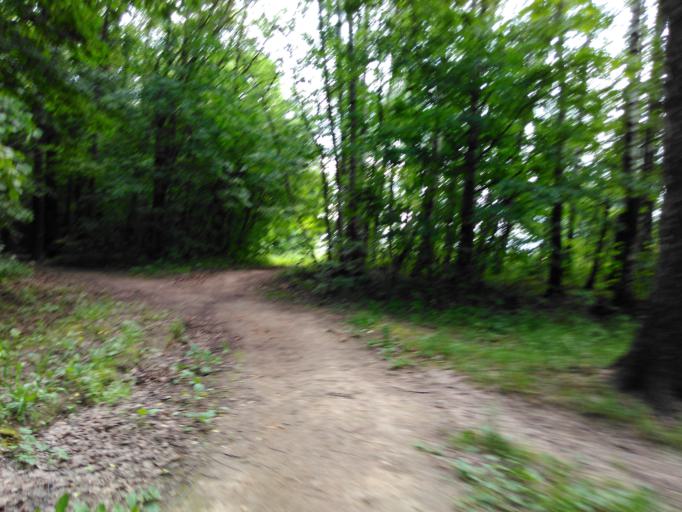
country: RU
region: Moscow
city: Zyuzino
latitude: 55.6331
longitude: 37.5430
